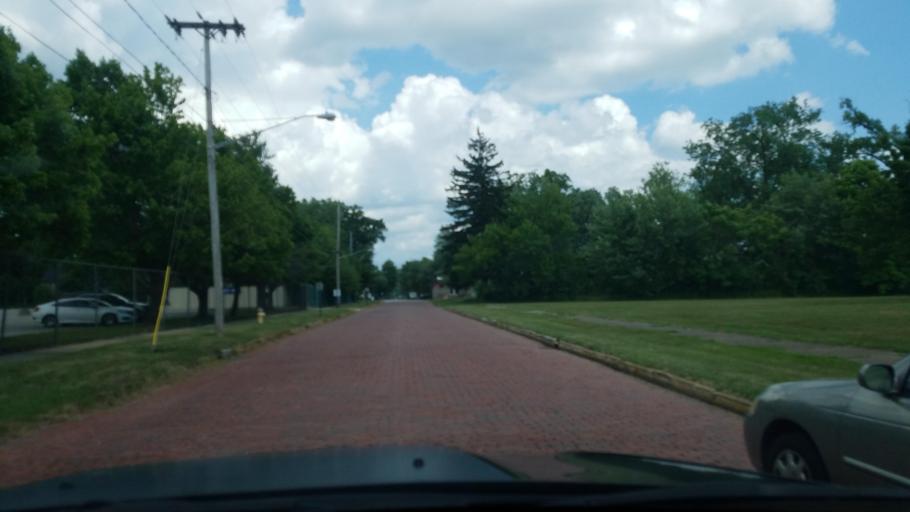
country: US
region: Ohio
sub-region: Trumbull County
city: Warren
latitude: 41.2343
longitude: -80.7985
